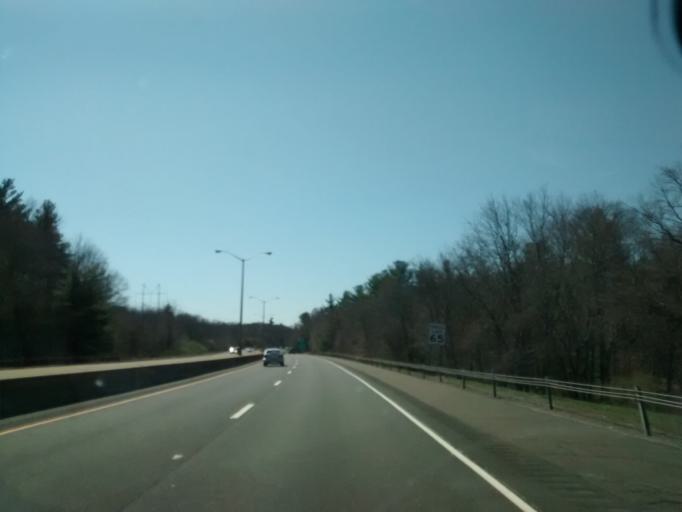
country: US
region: Connecticut
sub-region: Hartford County
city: East Hartford
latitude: 41.8039
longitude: -72.5970
